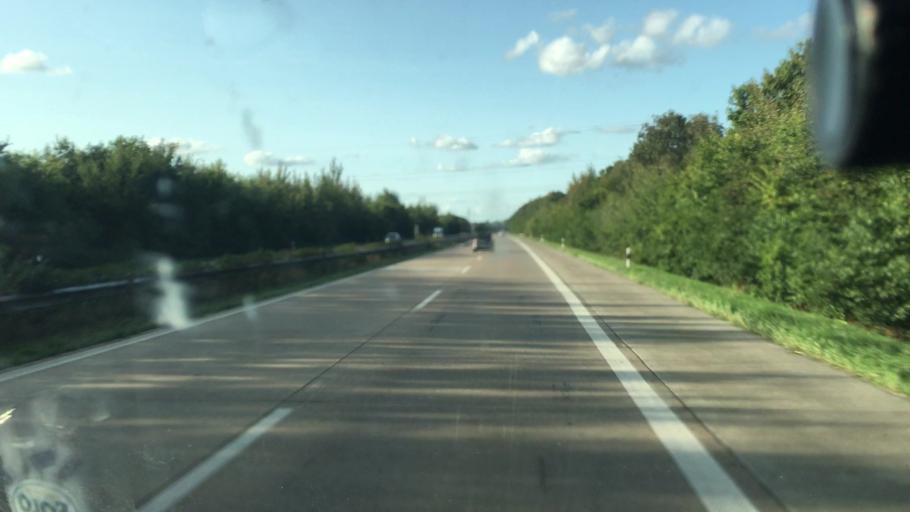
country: DE
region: Lower Saxony
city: Wiefelstede
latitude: 53.3106
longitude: 8.1434
